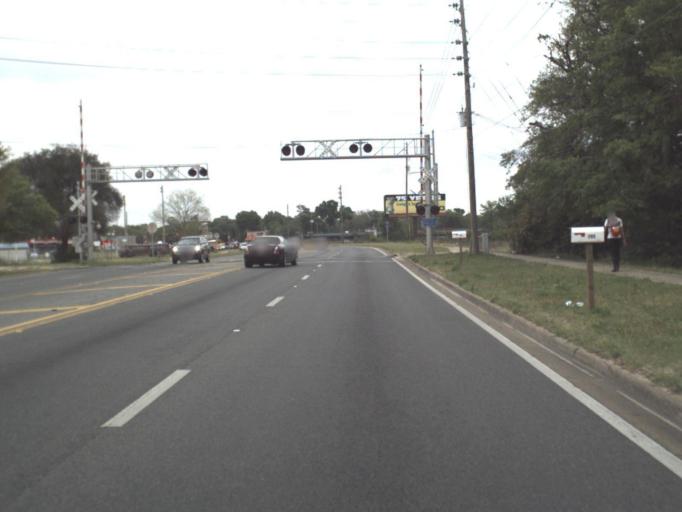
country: US
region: Florida
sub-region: Escambia County
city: Brent
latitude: 30.4636
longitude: -87.2568
